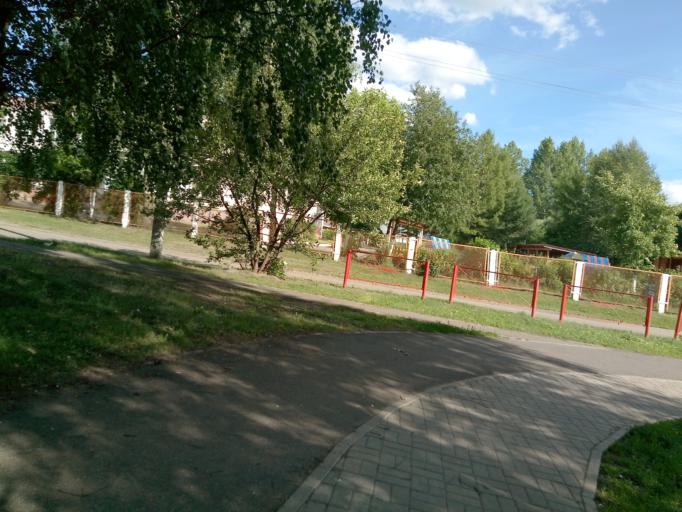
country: RU
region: Jaroslavl
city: Yaroslavl
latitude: 57.6557
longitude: 39.9547
